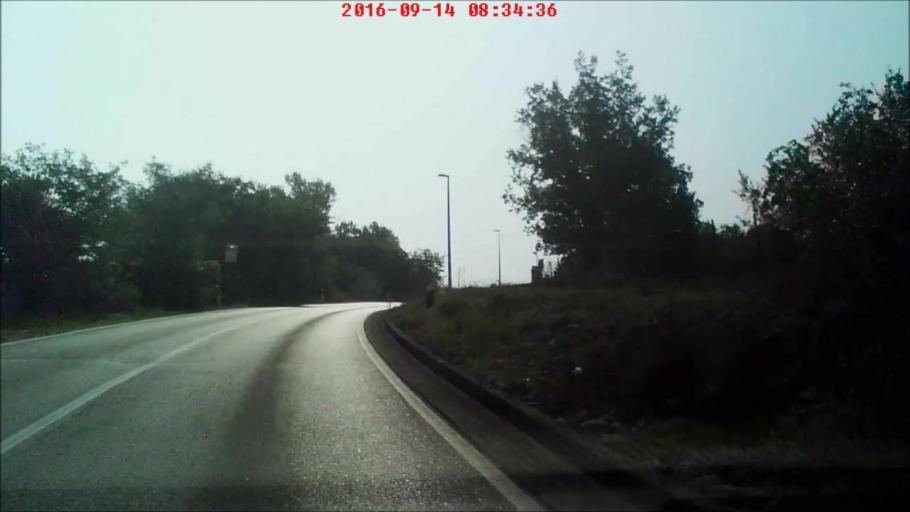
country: HR
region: Zadarska
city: Policnik
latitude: 44.1509
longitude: 15.3228
